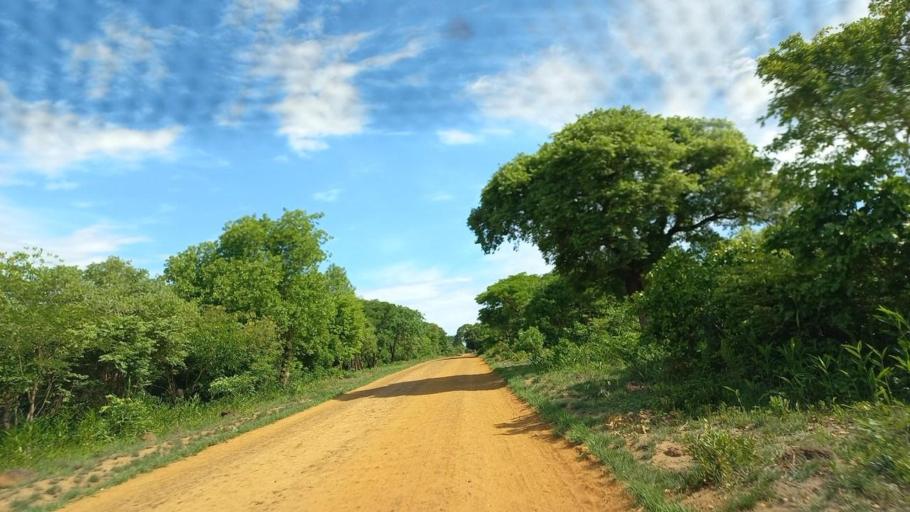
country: ZM
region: North-Western
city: Kabompo
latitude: -13.0657
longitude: 24.2187
